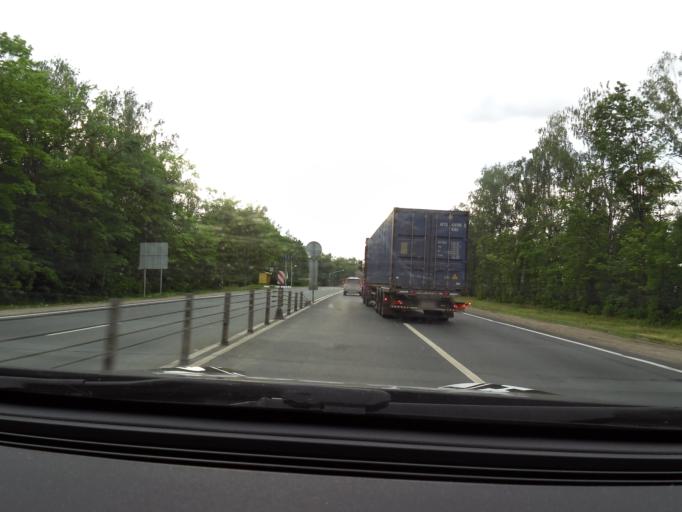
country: RU
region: Chuvashia
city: Tsivil'sk
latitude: 55.9154
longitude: 47.4151
